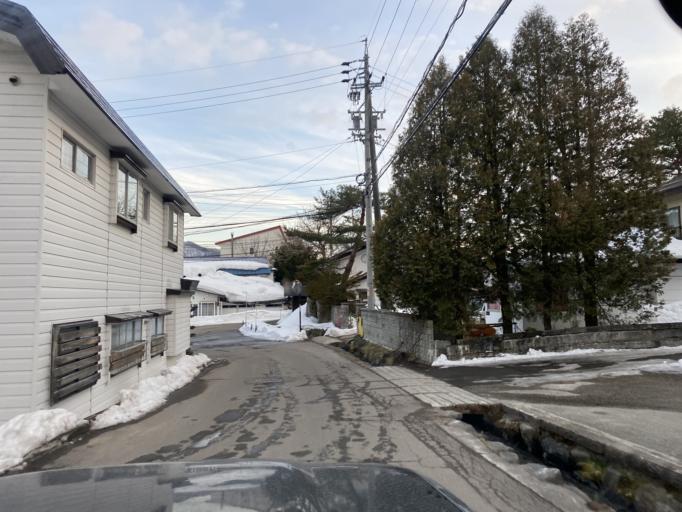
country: JP
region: Nagano
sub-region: Kitaazumi Gun
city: Hakuba
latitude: 36.7141
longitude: 137.8671
